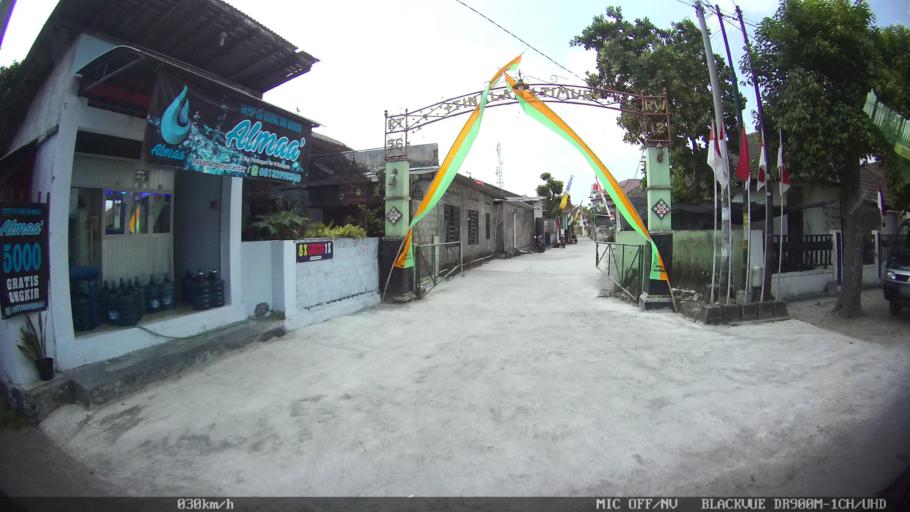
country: ID
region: Daerah Istimewa Yogyakarta
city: Yogyakarta
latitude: -7.8227
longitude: 110.3998
